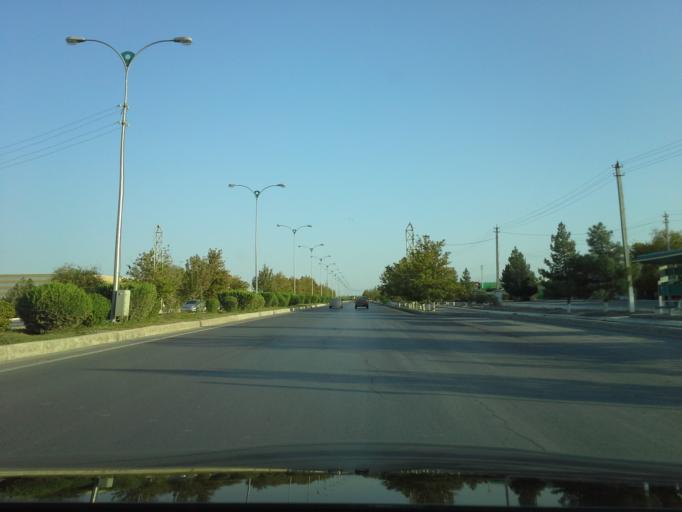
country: TM
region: Ahal
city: Abadan
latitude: 38.0300
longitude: 58.1941
